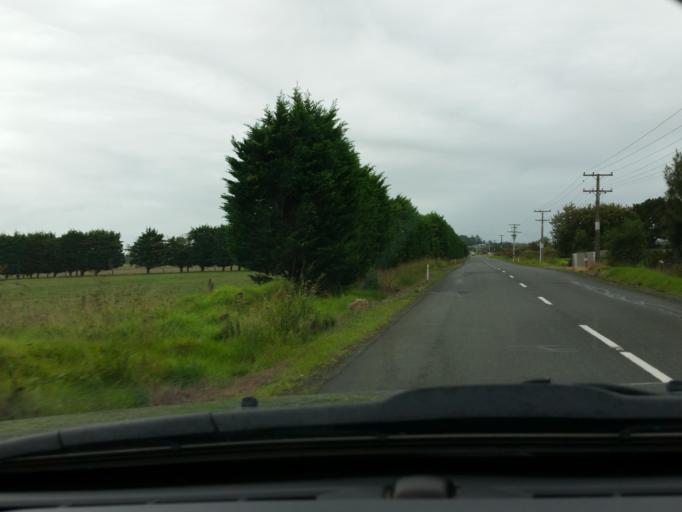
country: NZ
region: Northland
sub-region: Kaipara District
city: Dargaville
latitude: -35.9862
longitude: 173.8822
